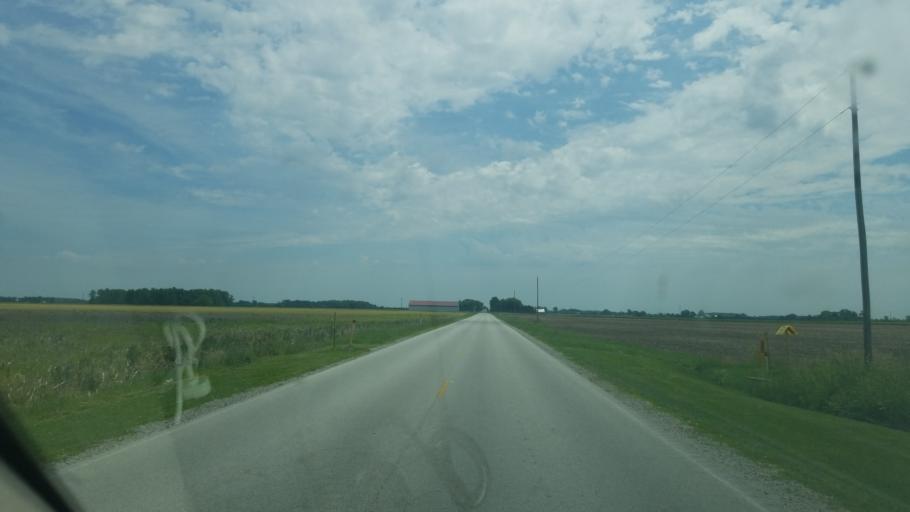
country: US
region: Ohio
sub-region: Wood County
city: Bowling Green
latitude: 41.2967
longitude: -83.6174
